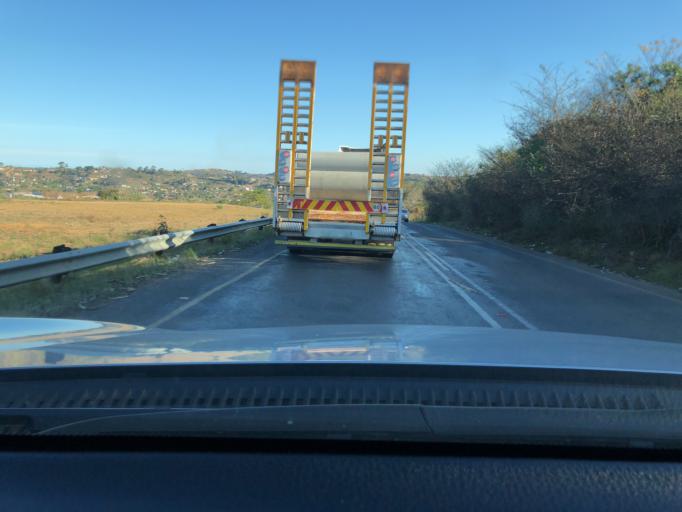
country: ZA
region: KwaZulu-Natal
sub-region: eThekwini Metropolitan Municipality
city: Umkomaas
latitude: -30.0310
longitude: 30.8112
